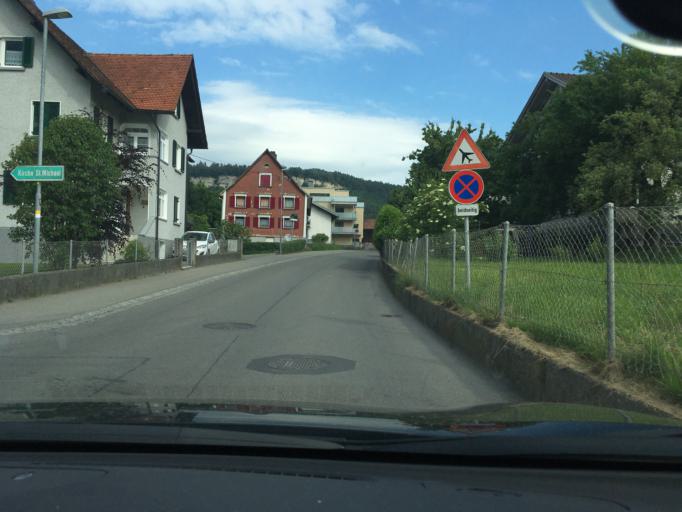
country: AT
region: Vorarlberg
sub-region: Politischer Bezirk Feldkirch
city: Feldkirch
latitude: 47.2298
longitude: 9.5785
